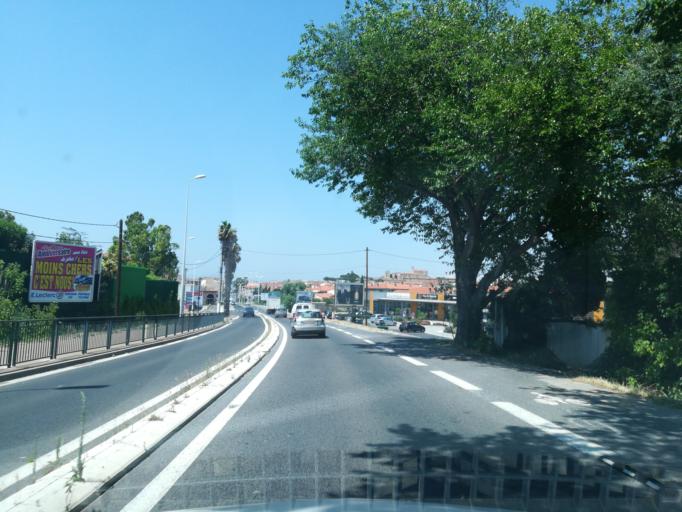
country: FR
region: Languedoc-Roussillon
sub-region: Departement des Pyrenees-Orientales
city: Perpignan
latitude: 42.6858
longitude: 2.8963
